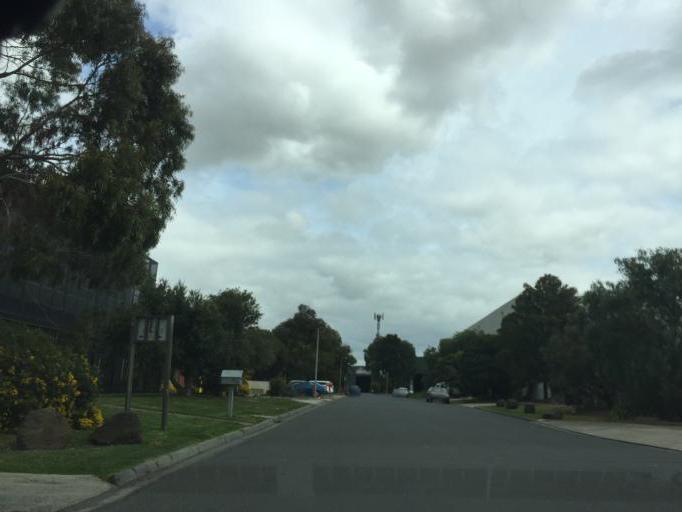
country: AU
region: Victoria
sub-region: Hobsons Bay
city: Altona North
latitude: -37.8228
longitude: 144.8564
